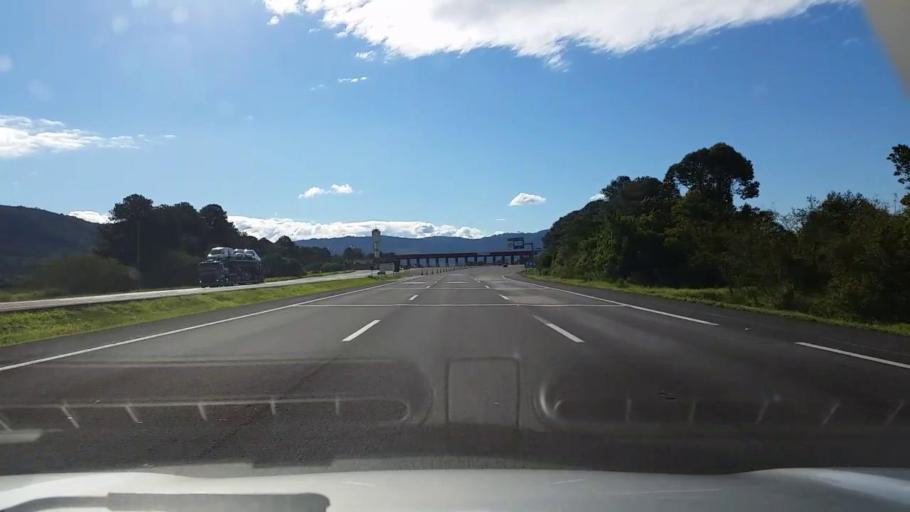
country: BR
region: Rio Grande do Sul
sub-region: Osorio
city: Osorio
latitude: -29.8866
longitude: -50.4511
